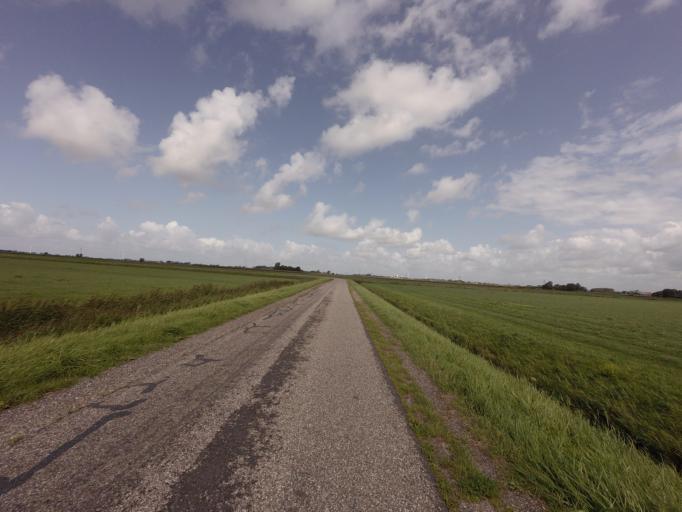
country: NL
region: Friesland
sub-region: Gemeente Franekeradeel
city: Sexbierum
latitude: 53.1643
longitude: 5.4862
